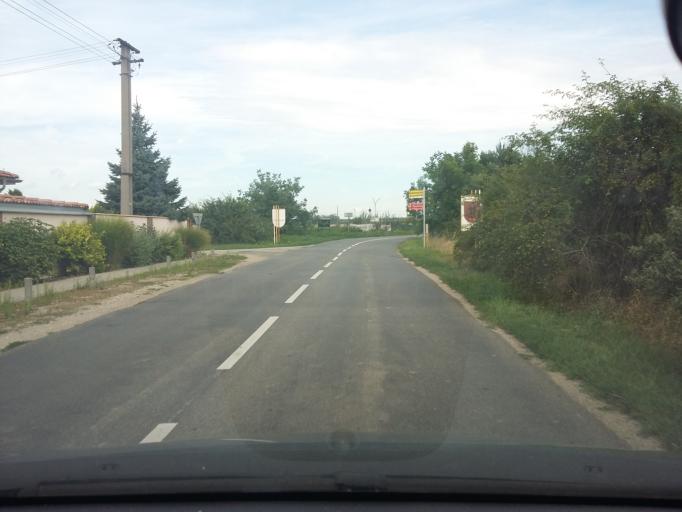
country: SK
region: Bratislavsky
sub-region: Okres Pezinok
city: Pezinok
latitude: 48.2572
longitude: 17.2854
